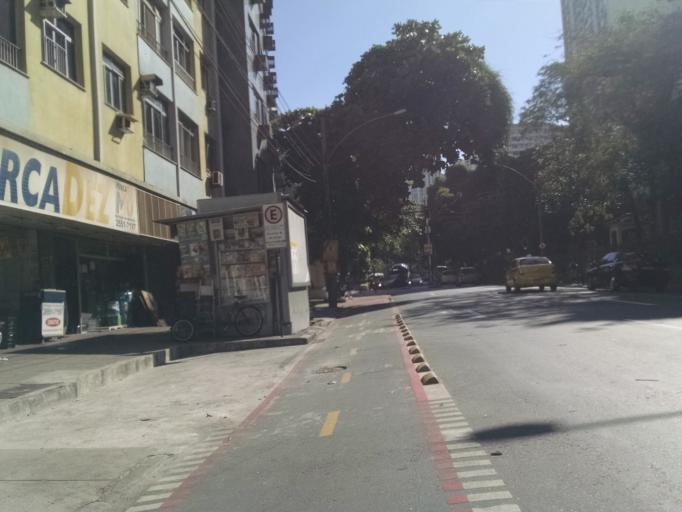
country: BR
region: Rio de Janeiro
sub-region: Rio De Janeiro
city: Rio de Janeiro
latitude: -22.9342
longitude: -43.1870
